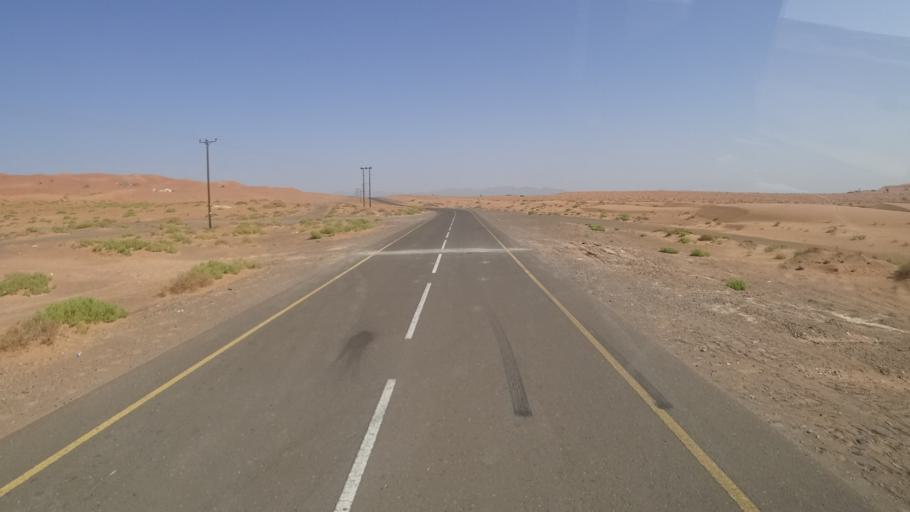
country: OM
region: Ash Sharqiyah
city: Al Qabil
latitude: 22.4872
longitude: 58.7146
